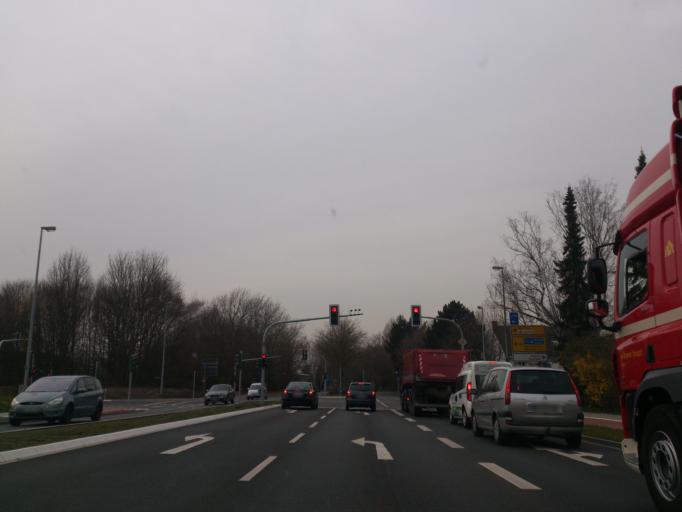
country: DE
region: North Rhine-Westphalia
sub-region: Regierungsbezirk Arnsberg
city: Soest
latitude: 51.5622
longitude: 8.1066
